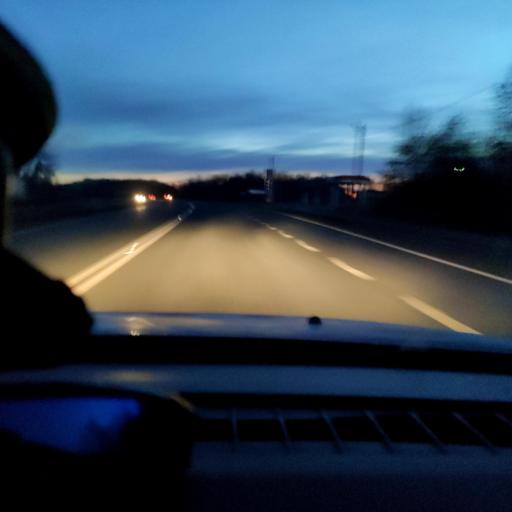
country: RU
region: Samara
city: Novokuybyshevsk
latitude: 52.9957
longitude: 49.9527
